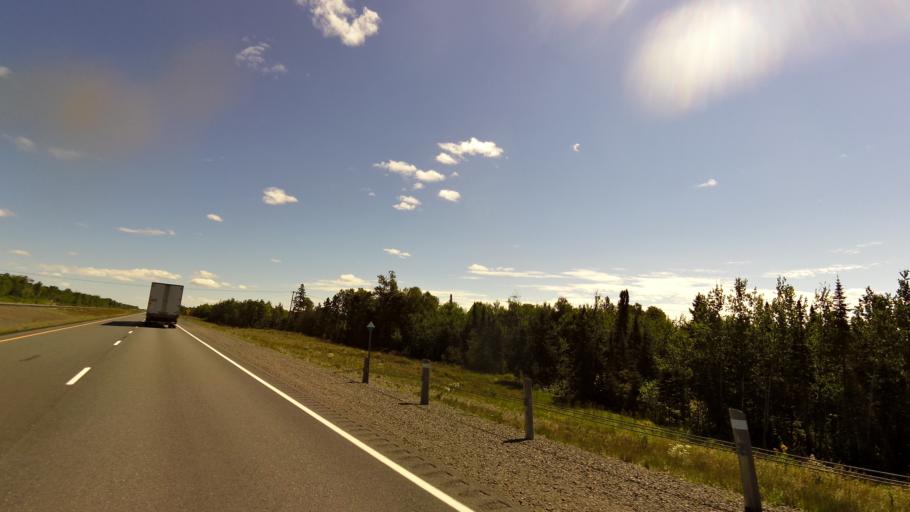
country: CA
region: Ontario
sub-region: Thunder Bay District
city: Thunder Bay
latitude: 48.5558
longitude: -88.8917
